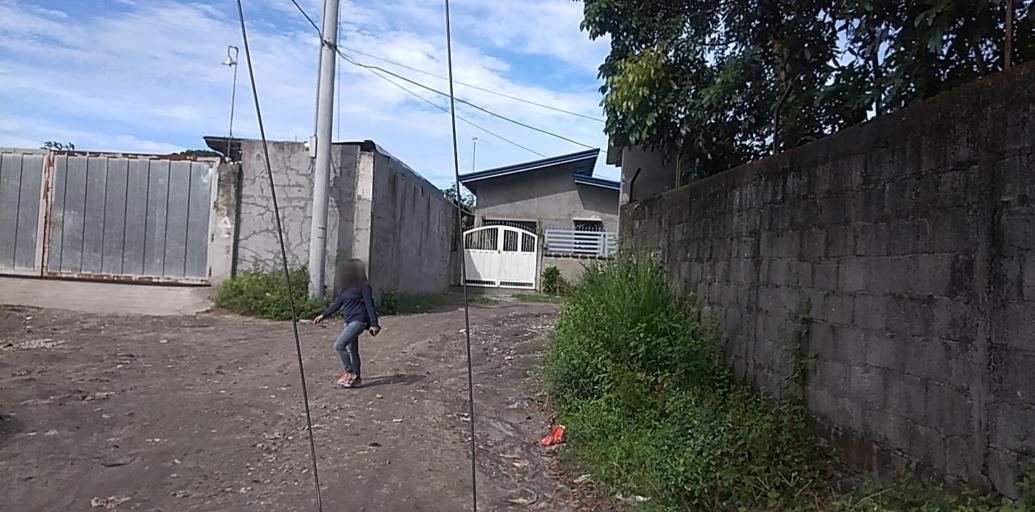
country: PH
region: Central Luzon
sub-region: Province of Pampanga
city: Manibaug Pasig
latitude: 15.1258
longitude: 120.5612
